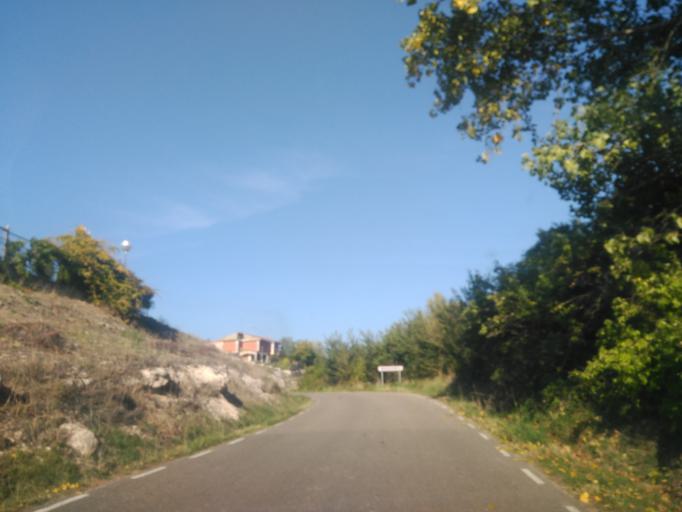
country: ES
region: Castille and Leon
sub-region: Provincia de Burgos
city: Brazacorta
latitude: 41.7159
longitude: -3.3683
